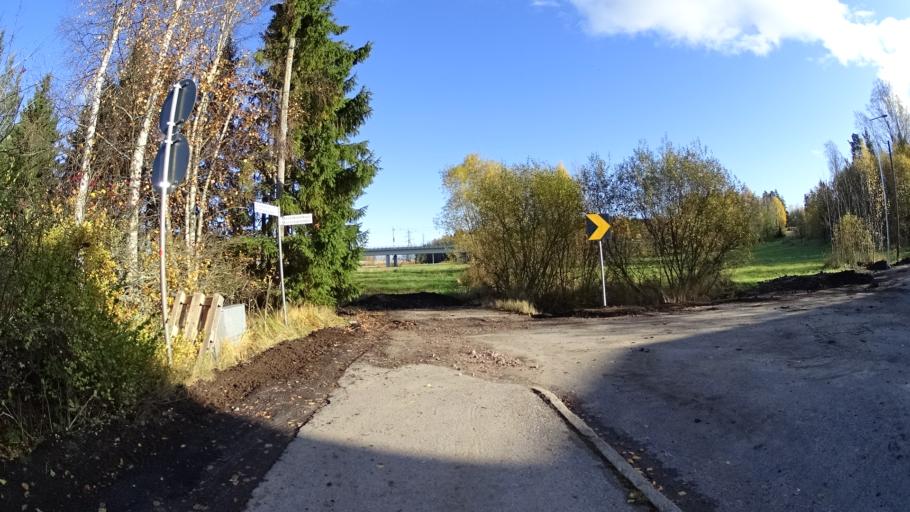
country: FI
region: Uusimaa
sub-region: Helsinki
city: Kilo
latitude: 60.2875
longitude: 24.8441
